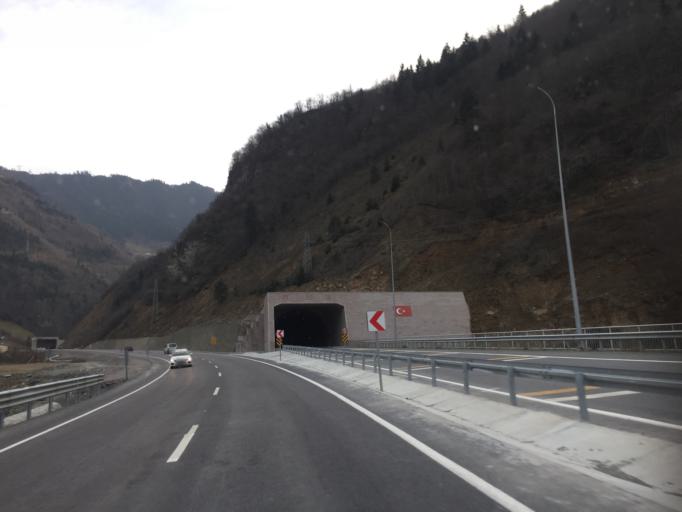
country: TR
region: Trabzon
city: Macka
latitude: 40.7580
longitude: 39.5625
